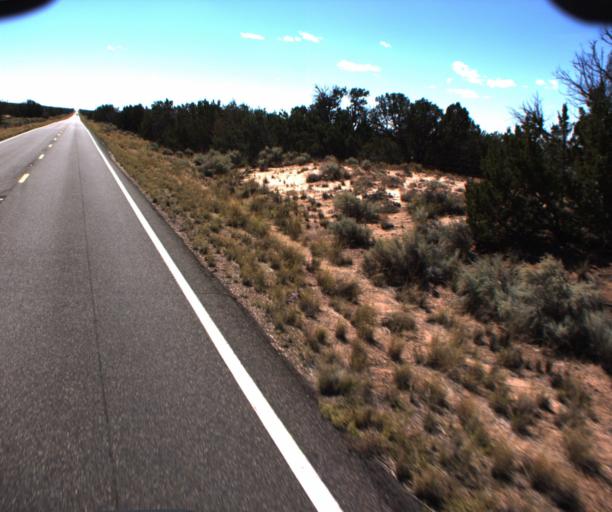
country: US
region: Arizona
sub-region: Apache County
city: Saint Johns
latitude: 34.8707
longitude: -109.2378
